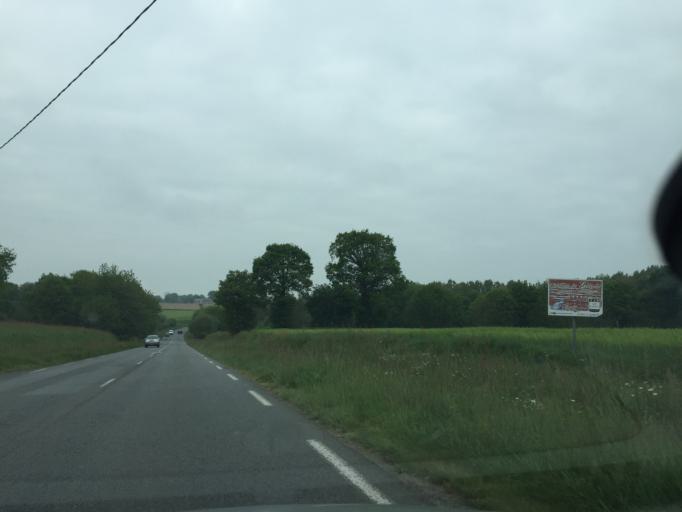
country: FR
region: Brittany
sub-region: Departement des Cotes-d'Armor
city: Crehen
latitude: 48.5858
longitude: -2.2387
